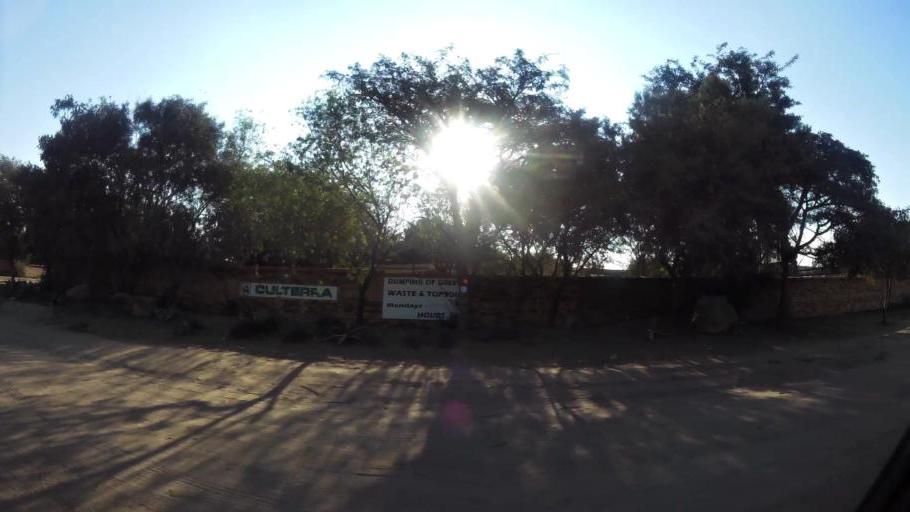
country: ZA
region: Gauteng
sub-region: City of Johannesburg Metropolitan Municipality
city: Diepsloot
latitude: -25.9809
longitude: 27.9420
